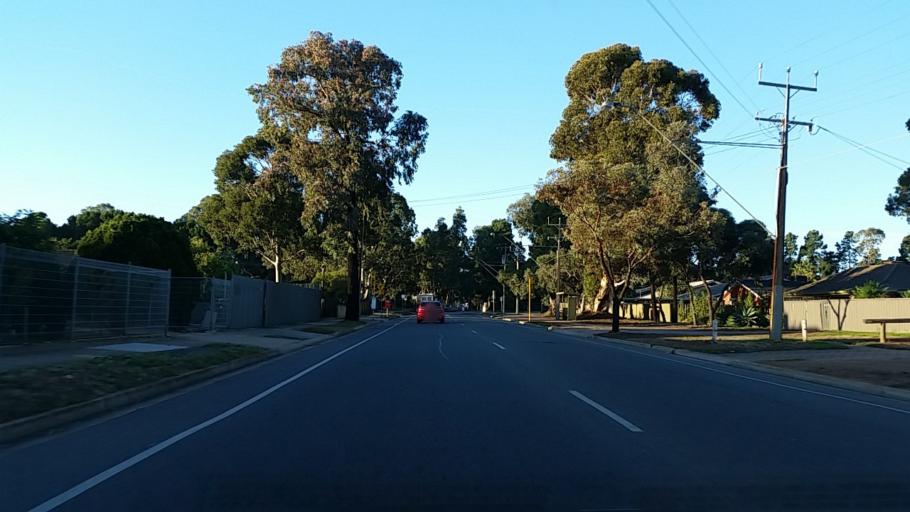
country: AU
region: South Australia
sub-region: Salisbury
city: Salisbury
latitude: -34.7612
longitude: 138.6583
